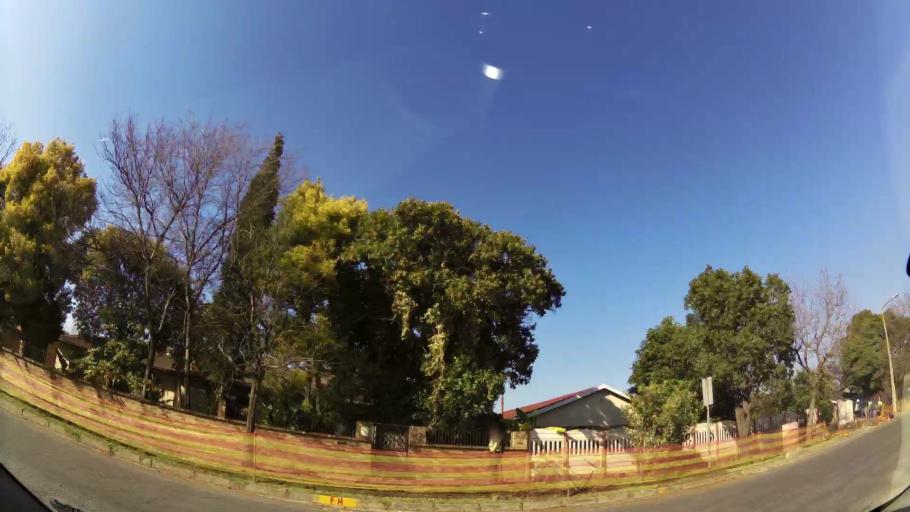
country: ZA
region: Gauteng
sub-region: Ekurhuleni Metropolitan Municipality
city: Benoni
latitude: -26.1539
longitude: 28.3044
